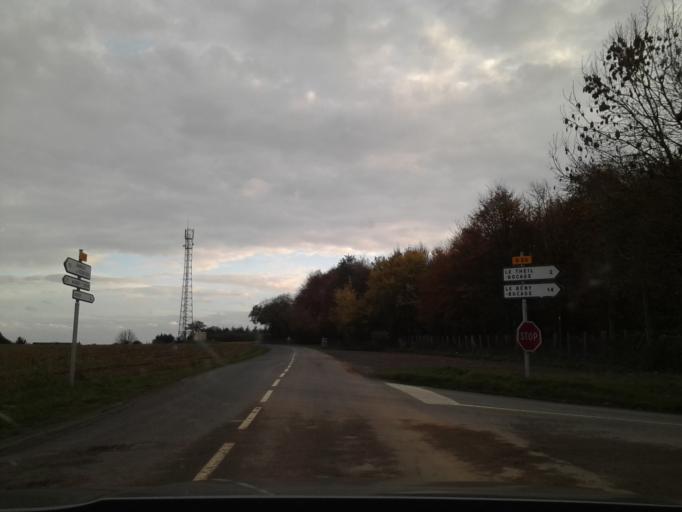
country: FR
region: Lower Normandy
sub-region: Departement du Calvados
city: Vassy
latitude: 48.8693
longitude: -0.6934
